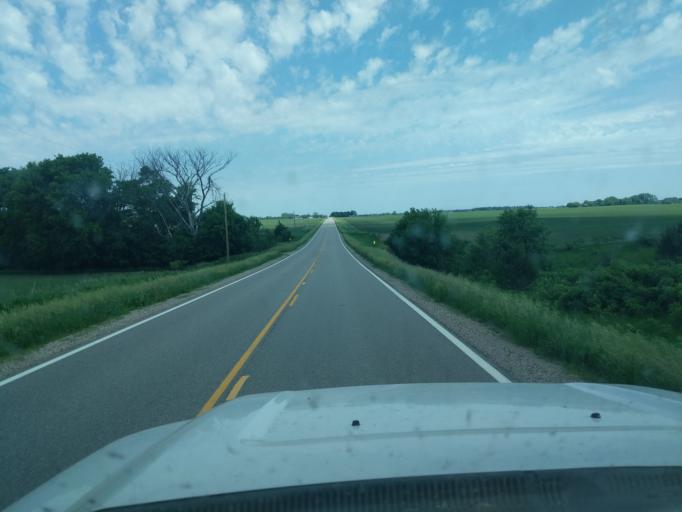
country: US
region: Minnesota
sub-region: Yellow Medicine County
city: Granite Falls
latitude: 44.7489
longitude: -95.4016
